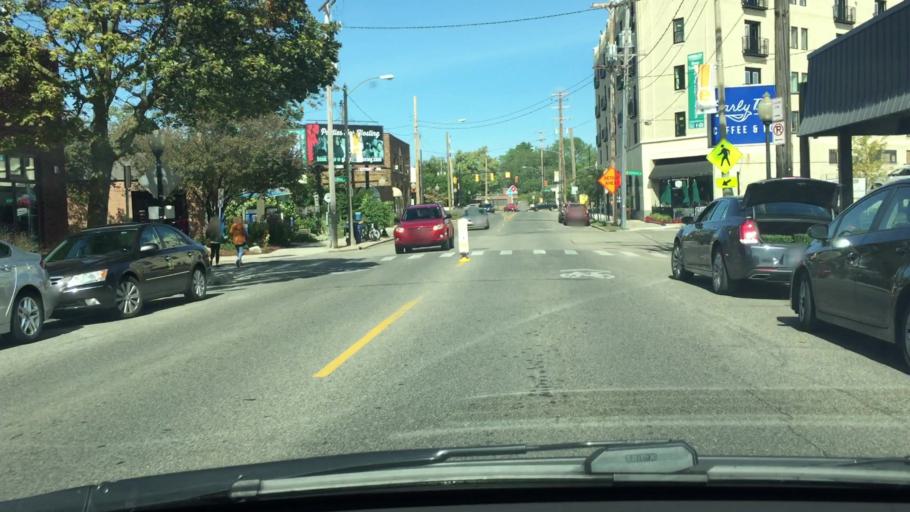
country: US
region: Michigan
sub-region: Kent County
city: East Grand Rapids
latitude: 42.9567
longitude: -85.6336
